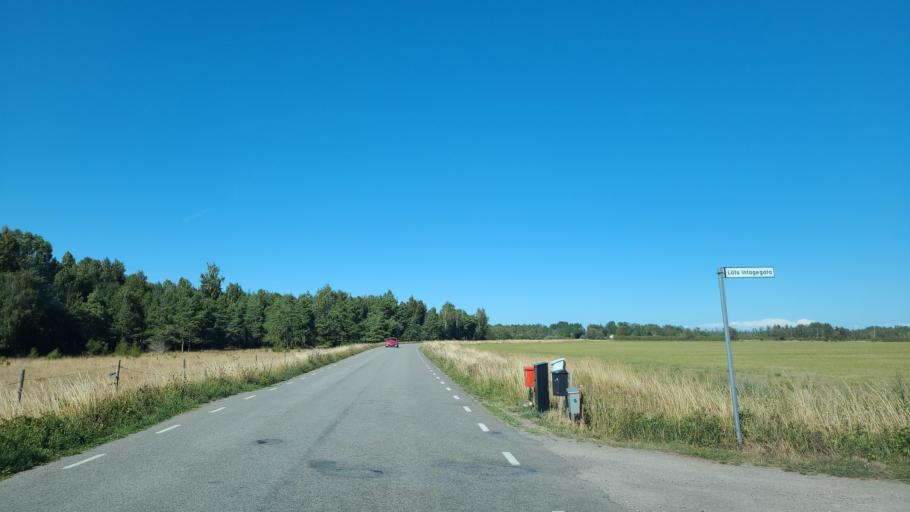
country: SE
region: Kalmar
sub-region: Borgholms Kommun
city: Borgholm
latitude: 56.9227
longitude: 16.8409
